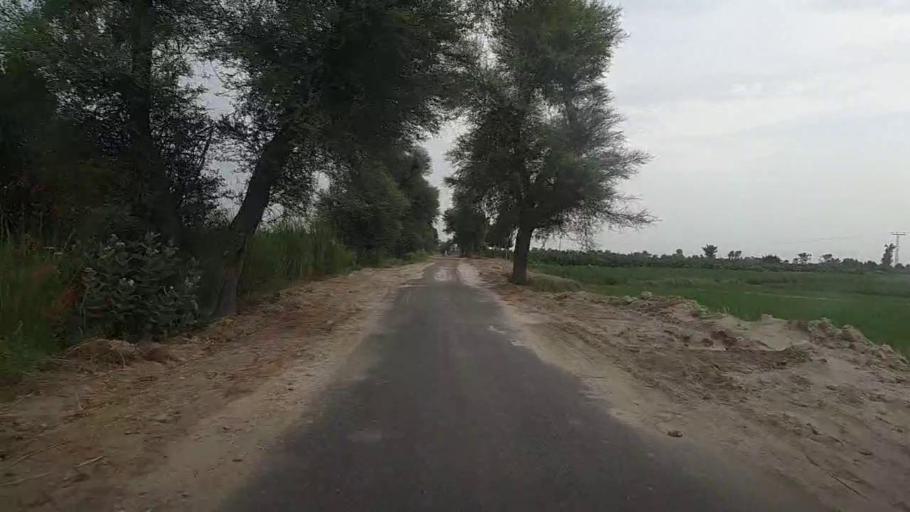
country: PK
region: Sindh
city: Karaundi
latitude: 26.9828
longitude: 68.3561
